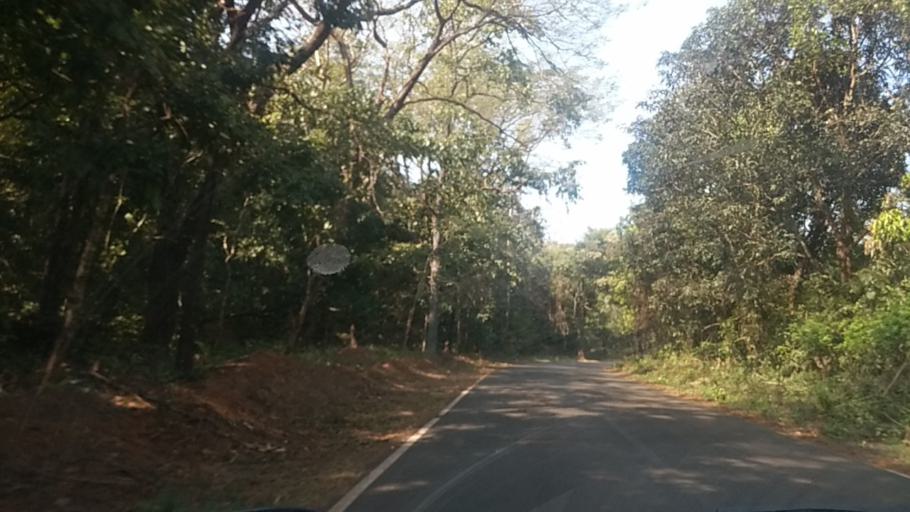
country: IN
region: Goa
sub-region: South Goa
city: Sanguem
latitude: 15.2125
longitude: 74.2061
